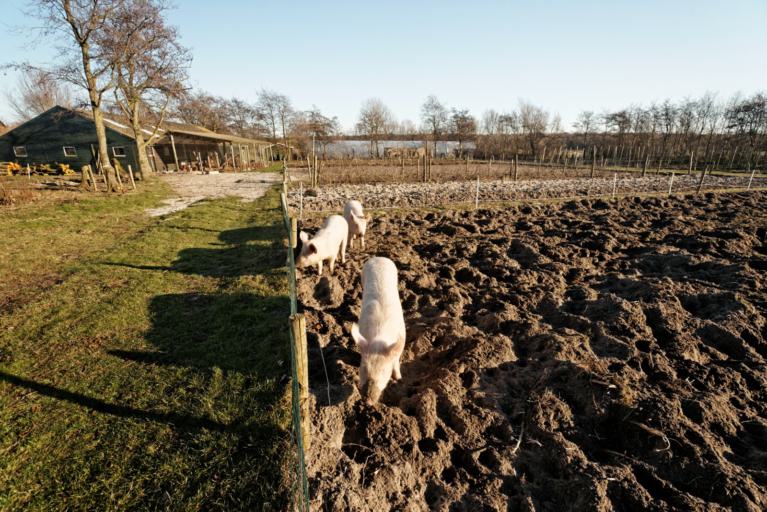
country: NL
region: North Holland
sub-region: Gemeente Texel
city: Den Burg
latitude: 53.0883
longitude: 4.7560
